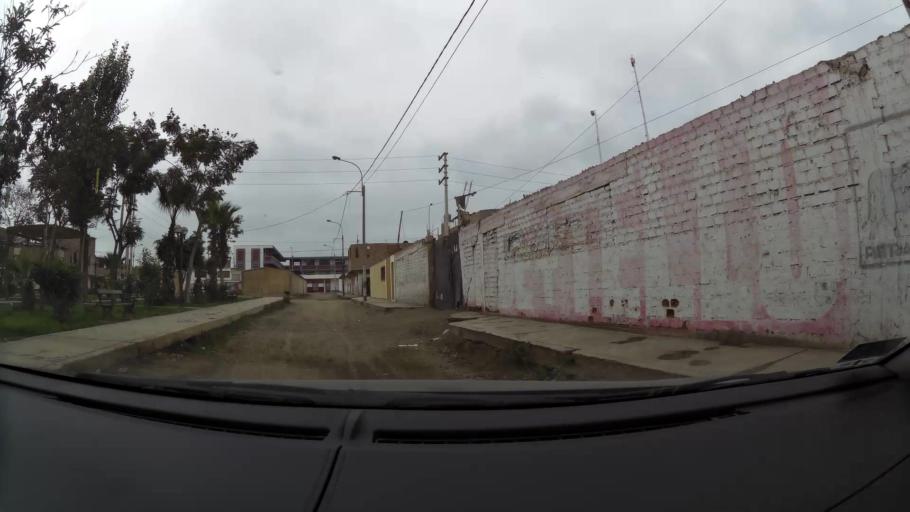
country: PE
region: Lima
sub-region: Provincia de Huaral
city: Huaral
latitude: -11.5015
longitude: -77.2145
